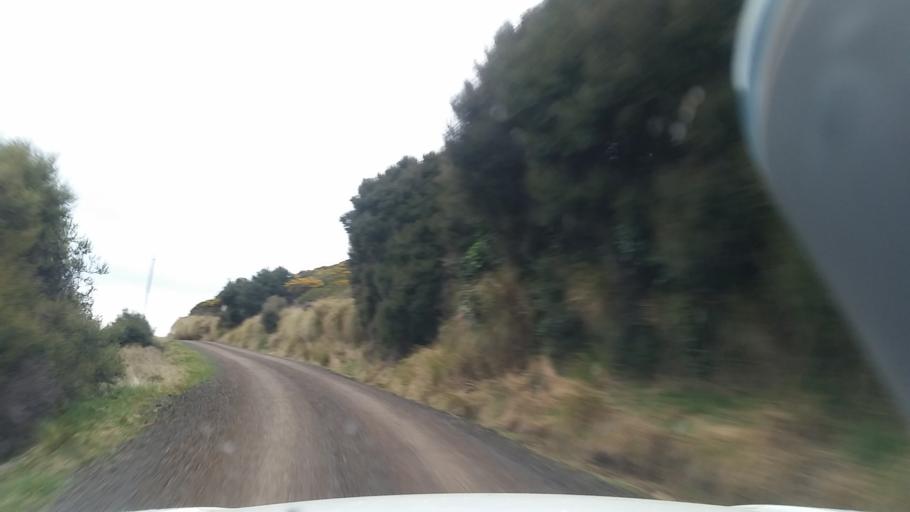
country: NZ
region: Canterbury
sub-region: Christchurch City
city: Christchurch
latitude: -43.8453
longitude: 172.9751
